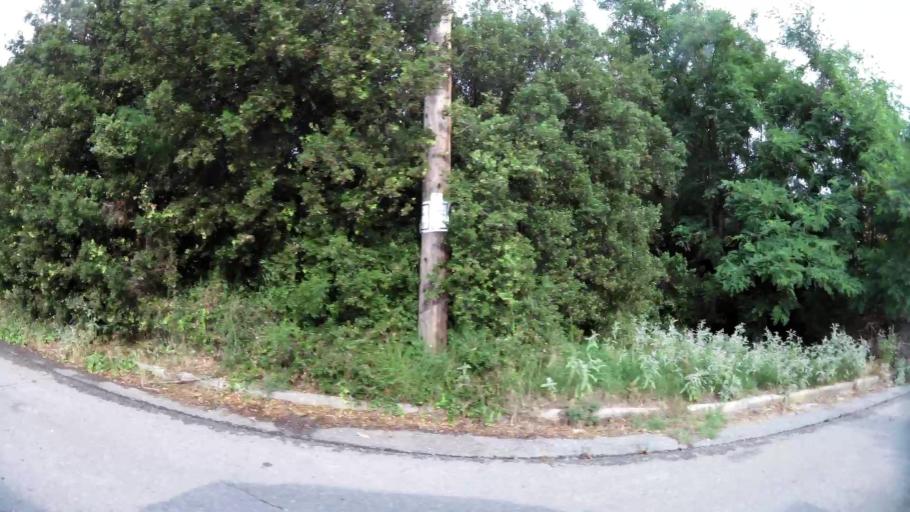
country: GR
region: Central Macedonia
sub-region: Nomos Thessalonikis
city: Oraiokastro
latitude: 40.7313
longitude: 22.9127
